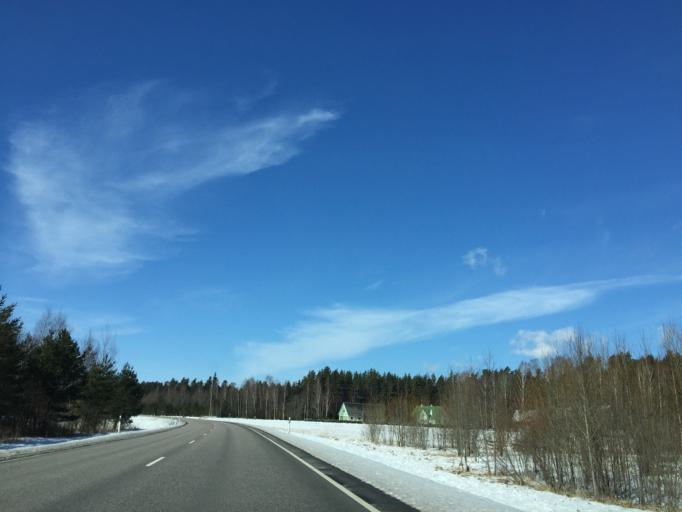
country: EE
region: Paernumaa
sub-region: Audru vald
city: Audru
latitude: 58.4226
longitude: 24.3495
